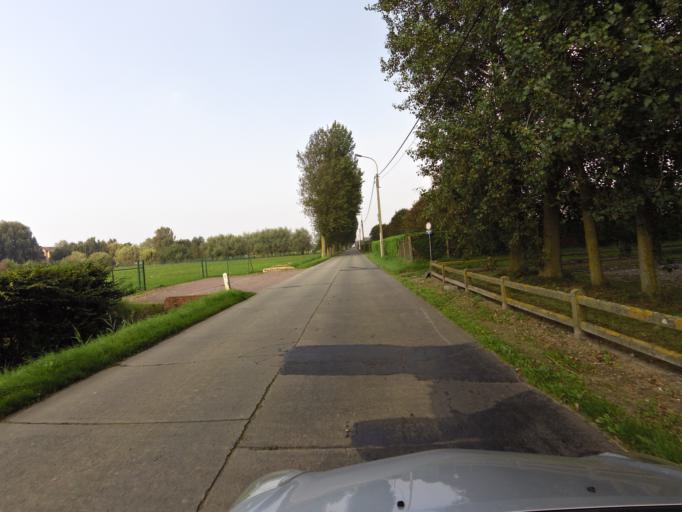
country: BE
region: Flanders
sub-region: Provincie West-Vlaanderen
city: Nieuwpoort
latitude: 51.1352
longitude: 2.7173
